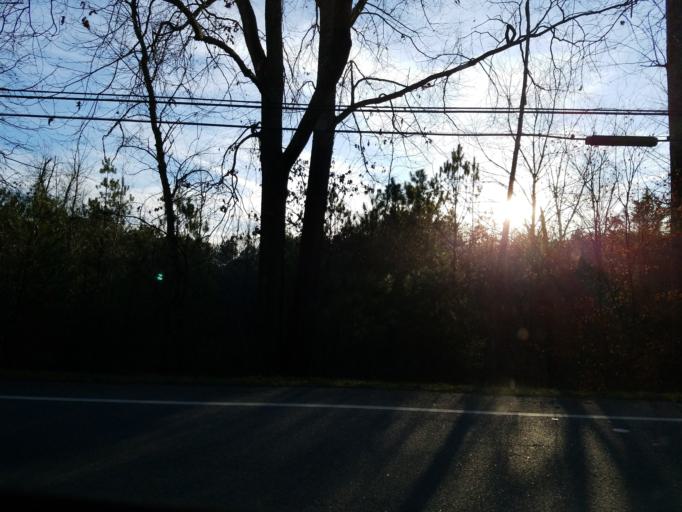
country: US
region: Georgia
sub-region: Gordon County
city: Calhoun
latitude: 34.6331
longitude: -84.9604
